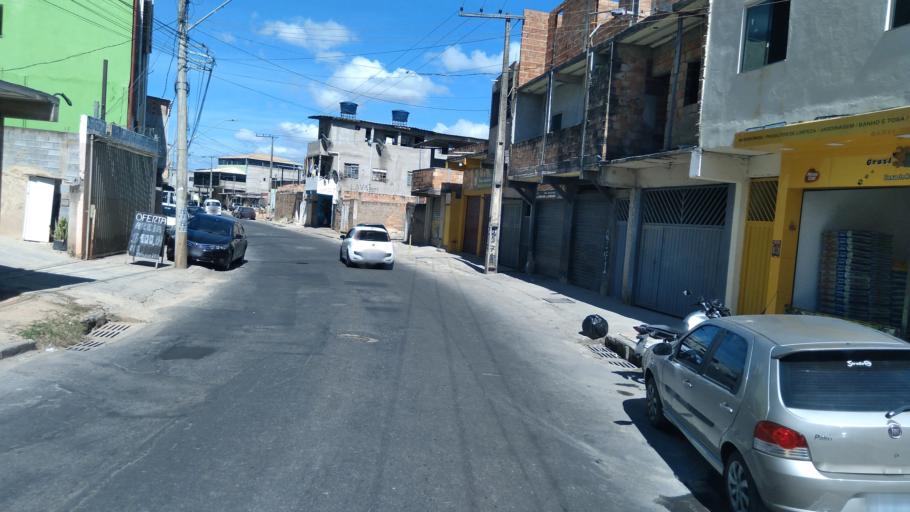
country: BR
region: Minas Gerais
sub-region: Belo Horizonte
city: Belo Horizonte
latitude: -19.8465
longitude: -43.9129
